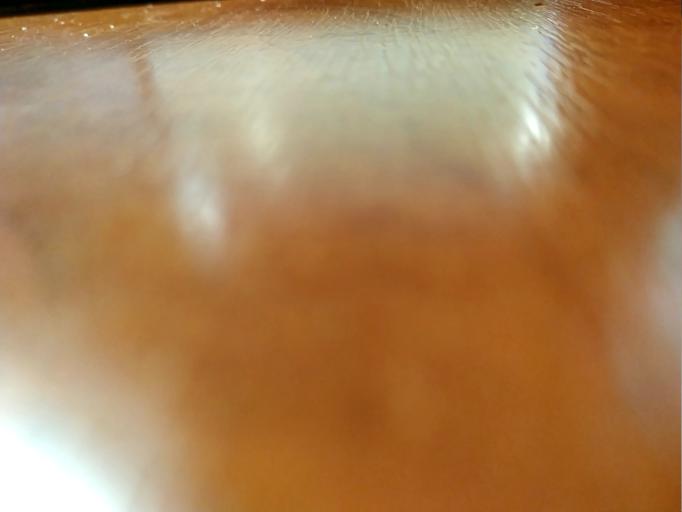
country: RU
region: Tverskaya
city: Sandovo
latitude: 58.4709
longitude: 36.3892
